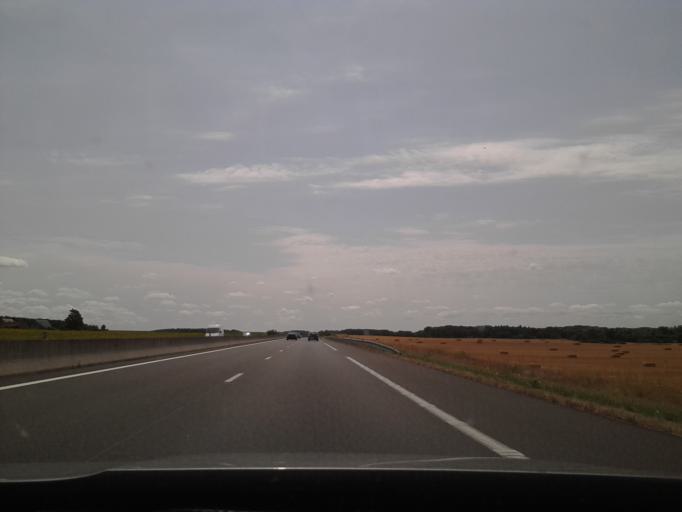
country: FR
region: Centre
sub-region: Departement d'Indre-et-Loire
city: Saint-Paterne-Racan
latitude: 47.6093
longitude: 0.5285
